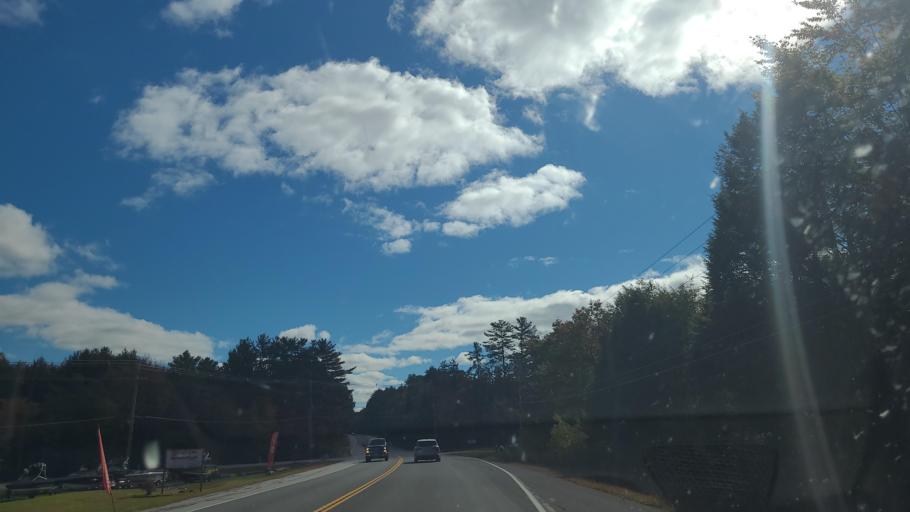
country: US
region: Maine
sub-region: Cumberland County
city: Bridgton
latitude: 43.9909
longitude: -70.6522
